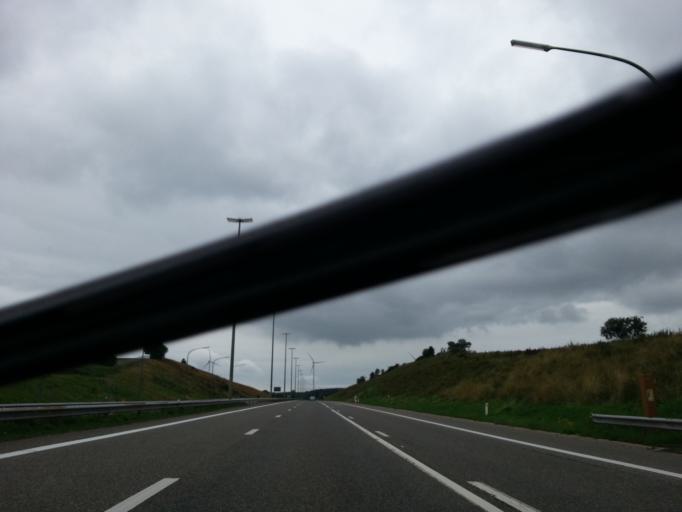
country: BE
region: Wallonia
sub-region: Province de Liege
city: Saint-Vith
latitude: 50.2915
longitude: 6.0942
